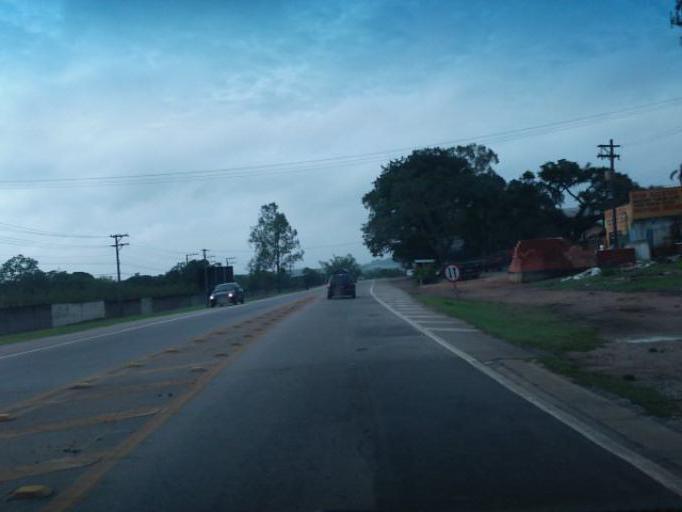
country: BR
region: Sao Paulo
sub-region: Sao Jose Dos Campos
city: Sao Jose dos Campos
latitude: -23.2297
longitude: -45.8706
